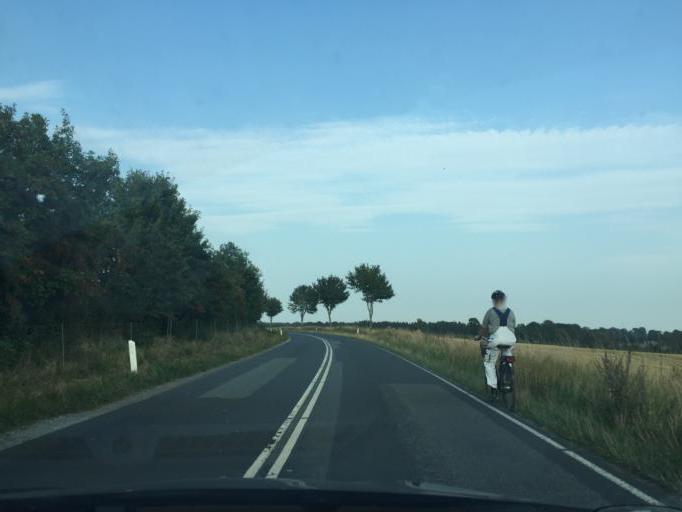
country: DK
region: South Denmark
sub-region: Kerteminde Kommune
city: Langeskov
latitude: 55.2873
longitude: 10.5522
